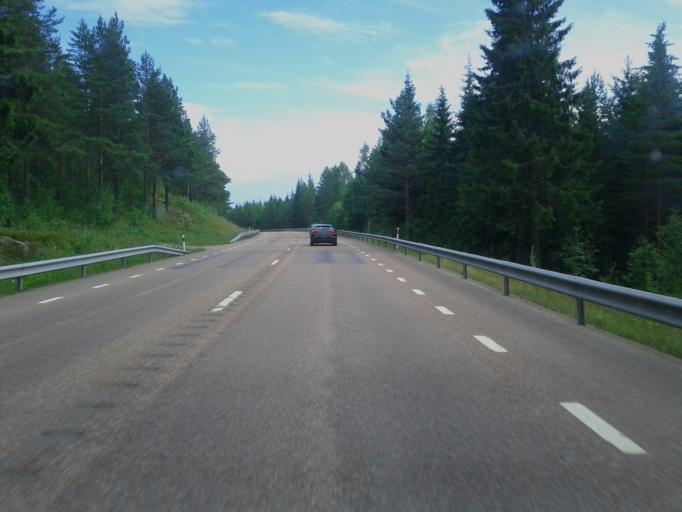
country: SE
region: Dalarna
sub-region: Faluns Kommun
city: Grycksbo
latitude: 60.7044
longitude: 15.4680
